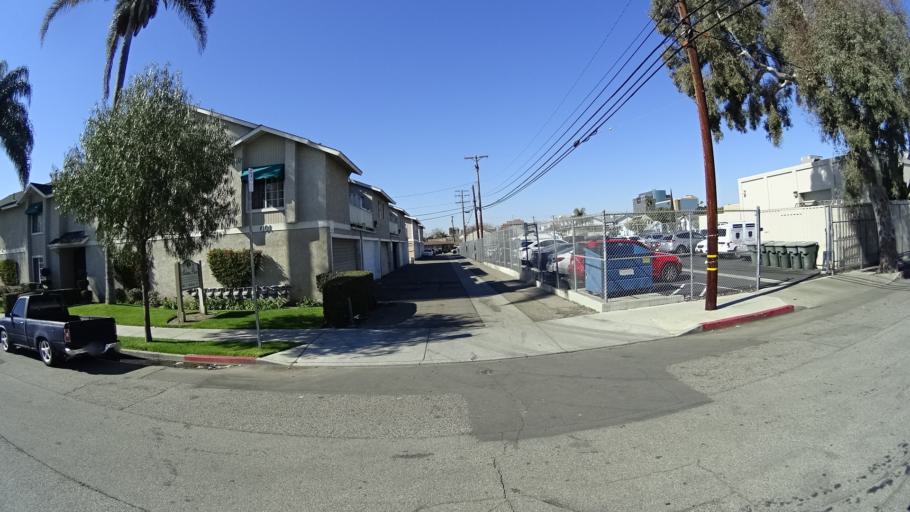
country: US
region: California
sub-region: Orange County
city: Anaheim
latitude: 33.8335
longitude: -117.9080
